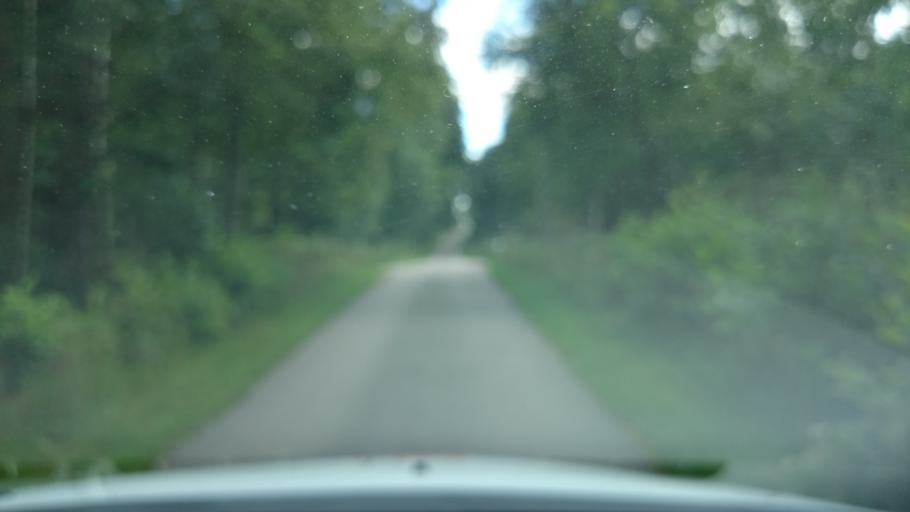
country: SE
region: Halland
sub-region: Hylte Kommun
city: Torup
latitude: 56.9561
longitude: 13.0934
